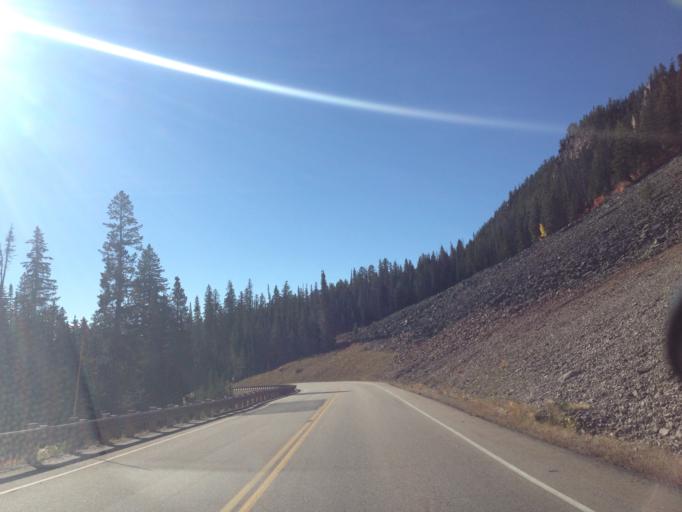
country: US
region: Montana
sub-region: Carbon County
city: Red Lodge
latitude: 45.0042
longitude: -109.8598
